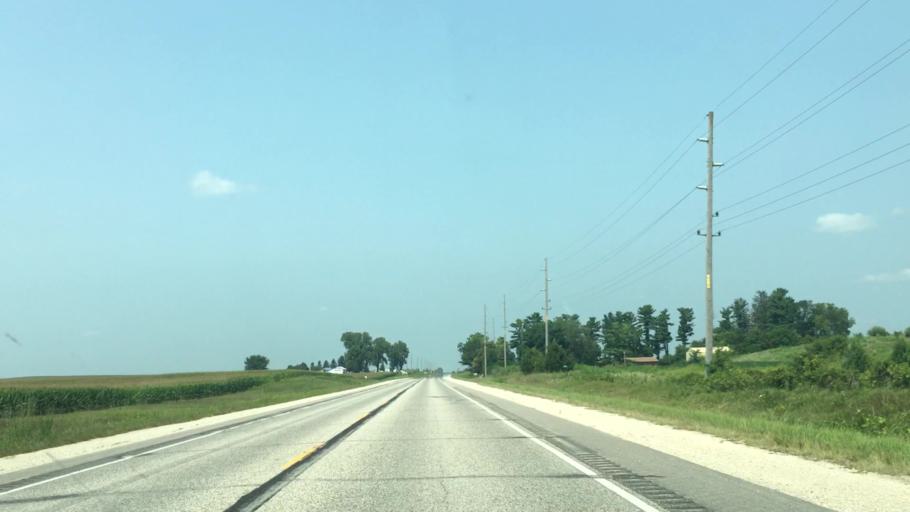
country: US
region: Iowa
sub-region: Fayette County
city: Fayette
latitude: 42.8778
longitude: -91.8105
